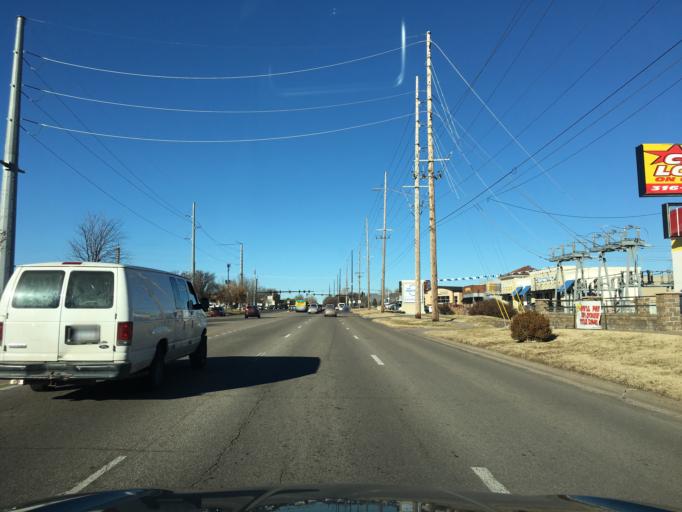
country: US
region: Kansas
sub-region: Sedgwick County
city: Bellaire
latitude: 37.6917
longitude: -97.2445
